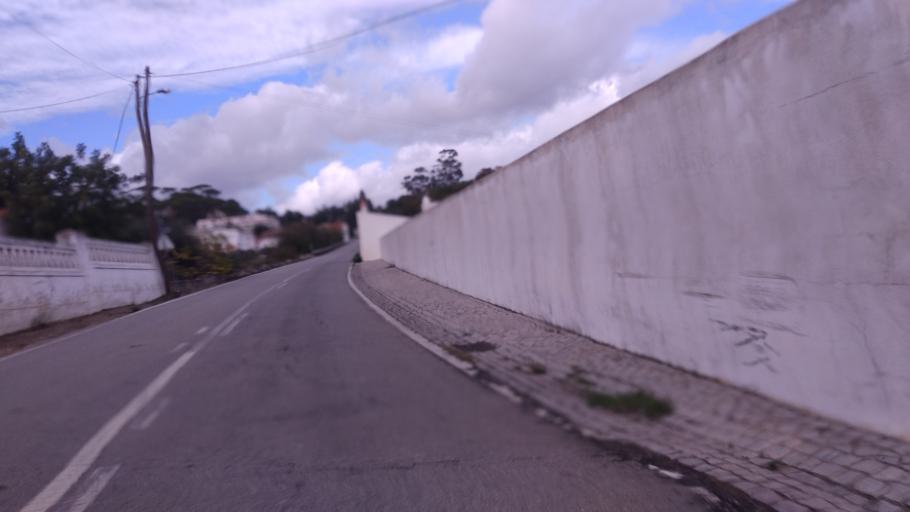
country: PT
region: Faro
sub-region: Sao Bras de Alportel
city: Sao Bras de Alportel
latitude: 37.1753
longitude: -7.9093
